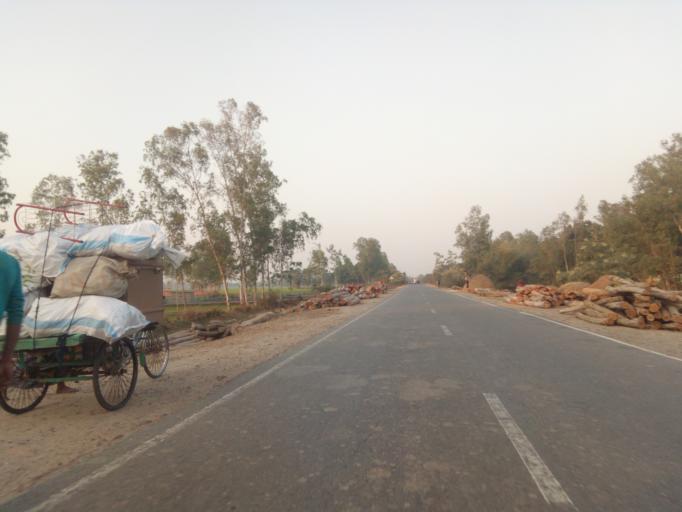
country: BD
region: Rajshahi
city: Bogra
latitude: 24.5953
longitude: 89.2374
